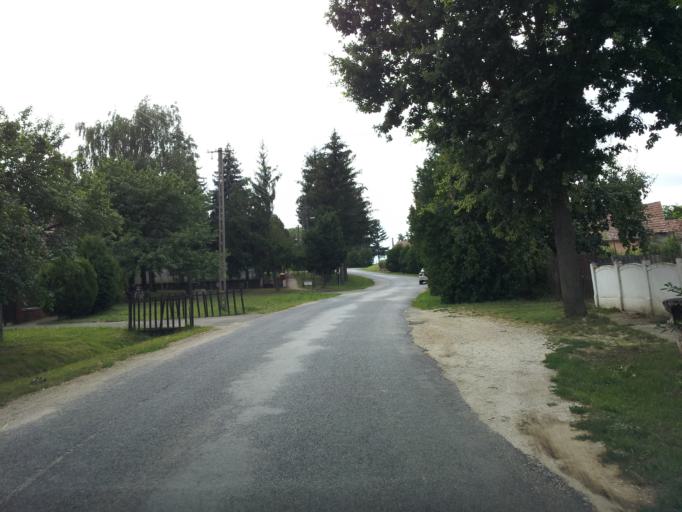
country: HU
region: Vas
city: Janoshaza
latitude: 47.1251
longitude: 17.1132
